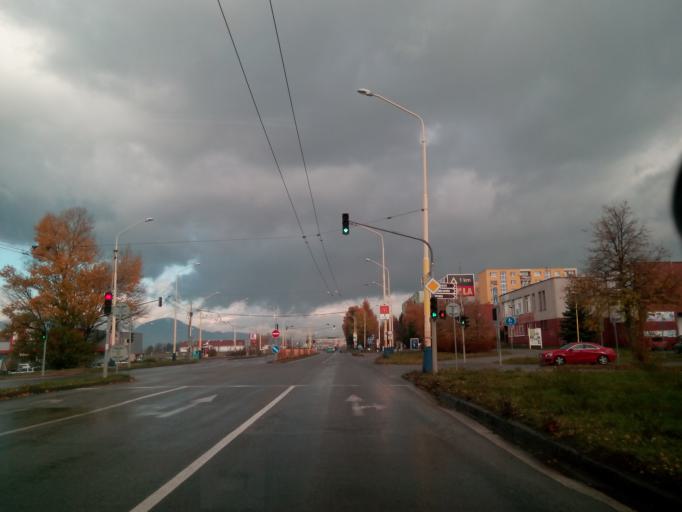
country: SK
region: Presovsky
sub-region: Okres Presov
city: Presov
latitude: 48.9860
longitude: 21.2643
